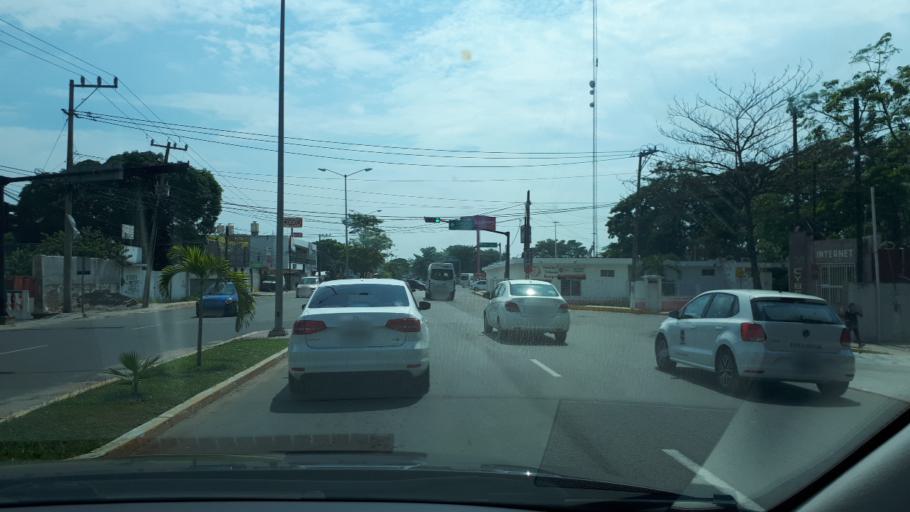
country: MX
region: Tabasco
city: Comalcalco
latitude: 18.2750
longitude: -93.2179
